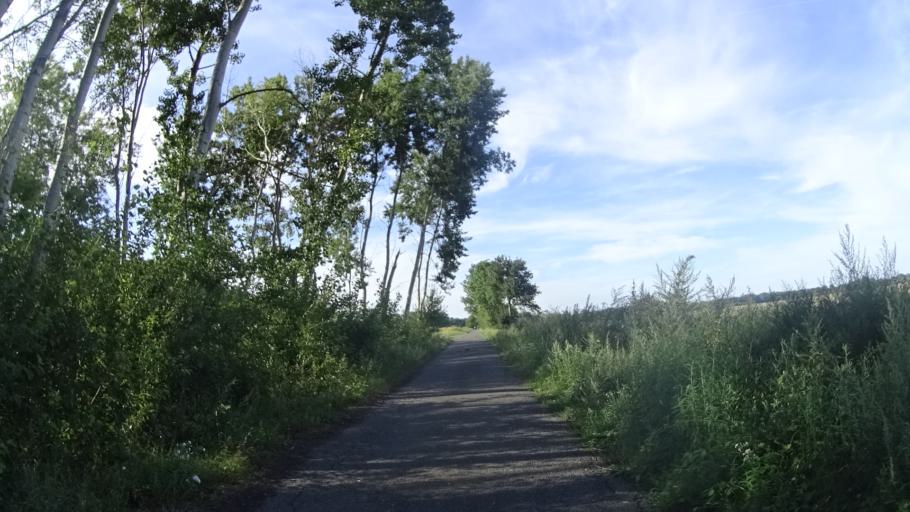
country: AT
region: Lower Austria
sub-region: Politischer Bezirk Ganserndorf
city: Drosing
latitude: 48.5847
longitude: 16.9518
